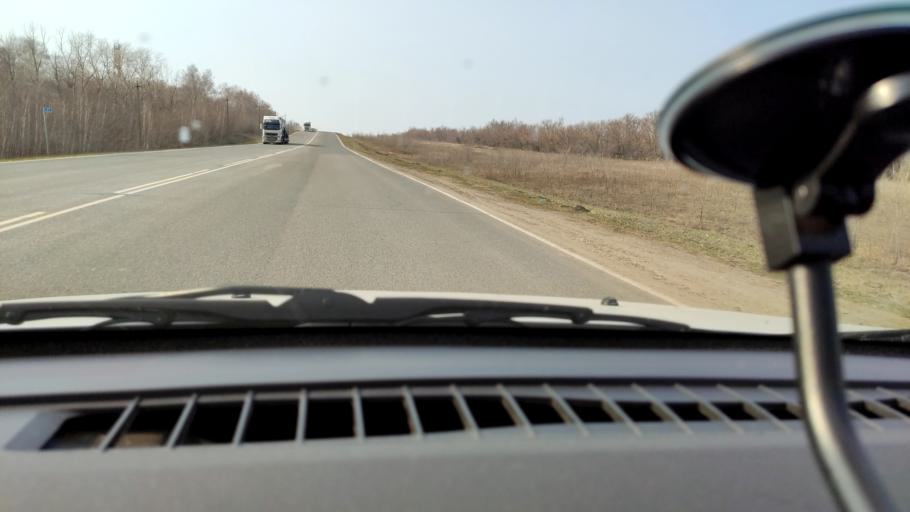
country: RU
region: Samara
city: Dubovyy Umet
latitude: 53.0740
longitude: 50.3578
